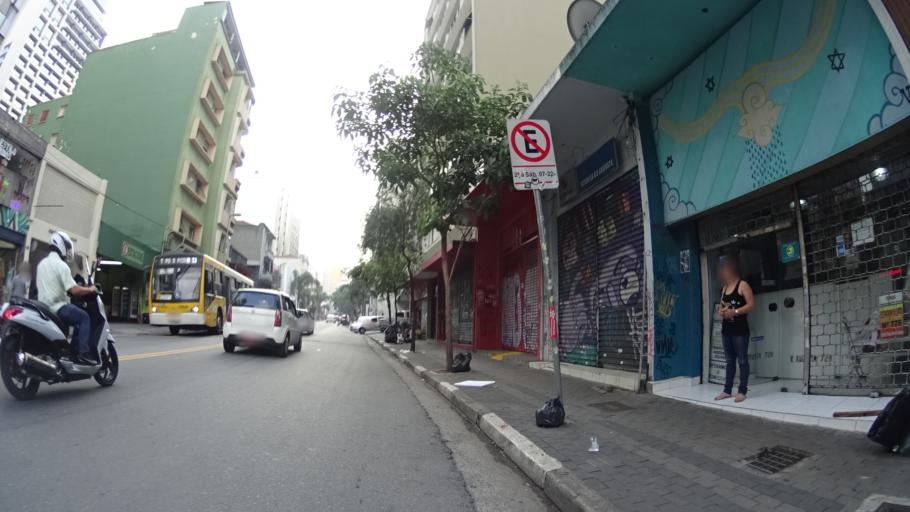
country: BR
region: Sao Paulo
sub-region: Sao Paulo
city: Sao Paulo
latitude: -23.5521
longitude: -46.6529
